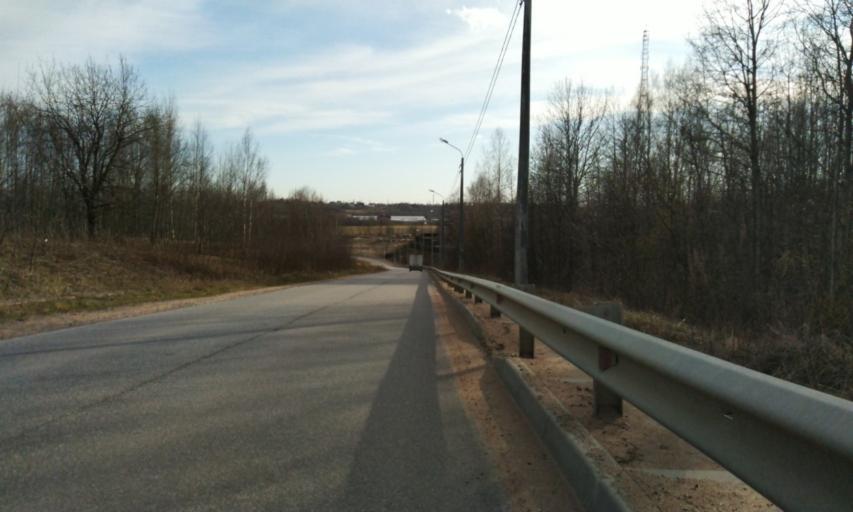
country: RU
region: Leningrad
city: Bugry
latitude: 60.1172
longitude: 30.4268
